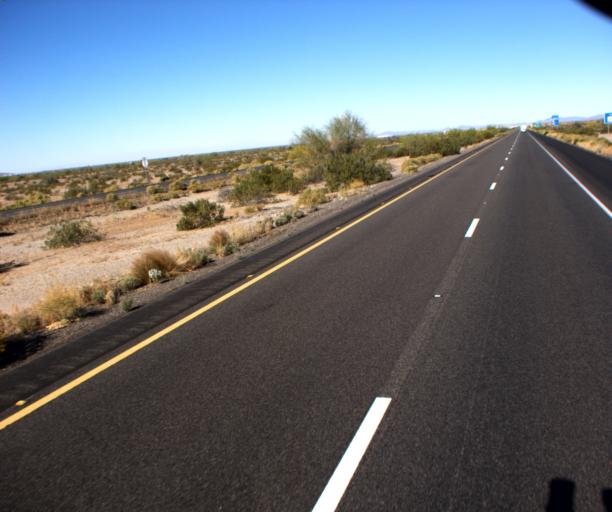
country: US
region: Arizona
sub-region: Maricopa County
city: Gila Bend
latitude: 32.9222
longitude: -112.6564
